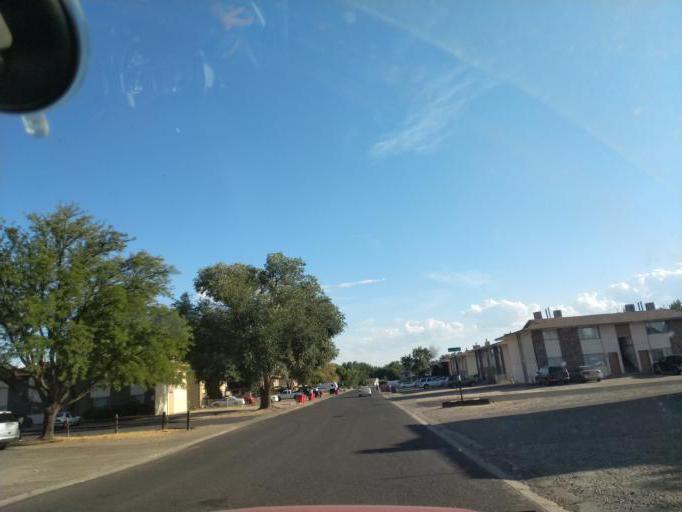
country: US
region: Colorado
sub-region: Mesa County
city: Clifton
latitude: 39.0759
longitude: -108.4566
